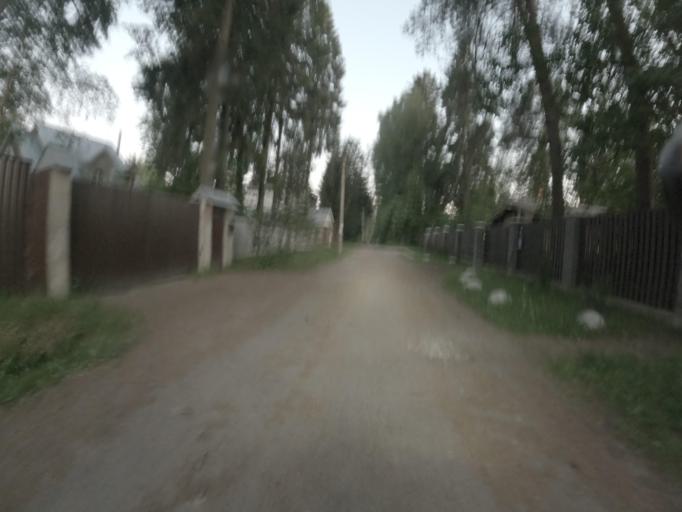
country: RU
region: Leningrad
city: Vsevolozhsk
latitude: 60.0173
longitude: 30.6158
